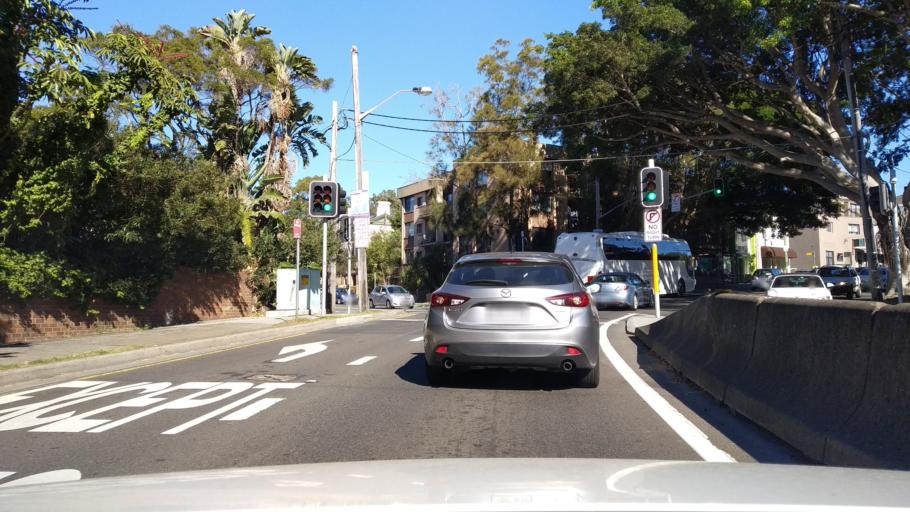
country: AU
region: New South Wales
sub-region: Waverley
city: Bondi
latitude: -33.8892
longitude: 151.2597
